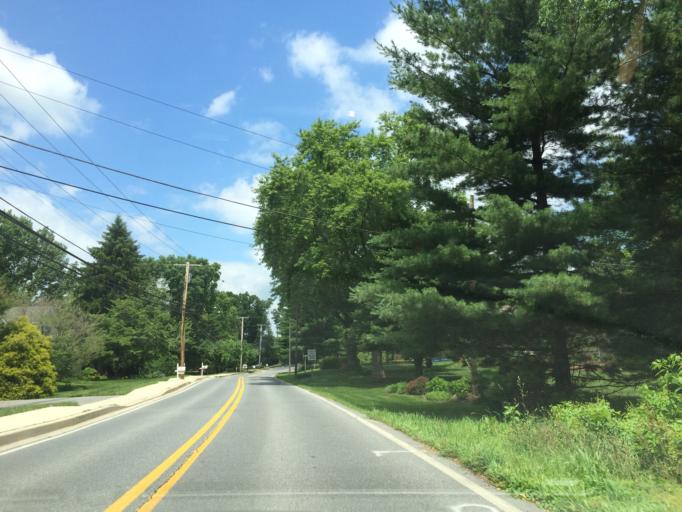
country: US
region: Maryland
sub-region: Howard County
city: Ellicott City
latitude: 39.2859
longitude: -76.8291
